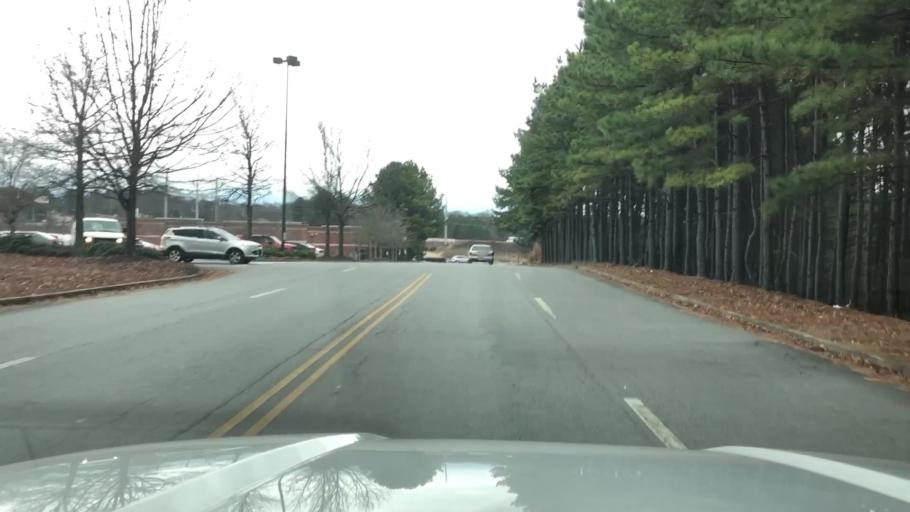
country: US
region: Georgia
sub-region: Cherokee County
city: Woodstock
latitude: 34.0829
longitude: -84.5441
